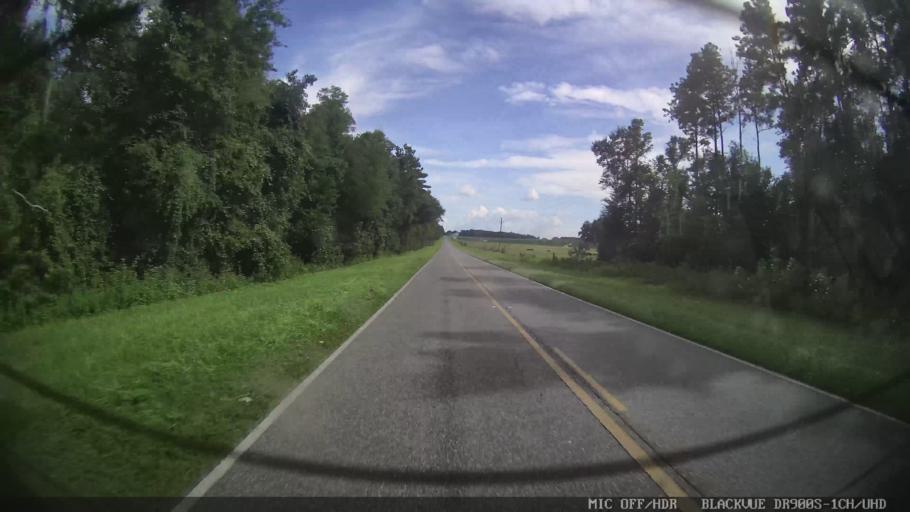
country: US
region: Georgia
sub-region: Echols County
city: Statenville
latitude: 30.5964
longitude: -83.2242
